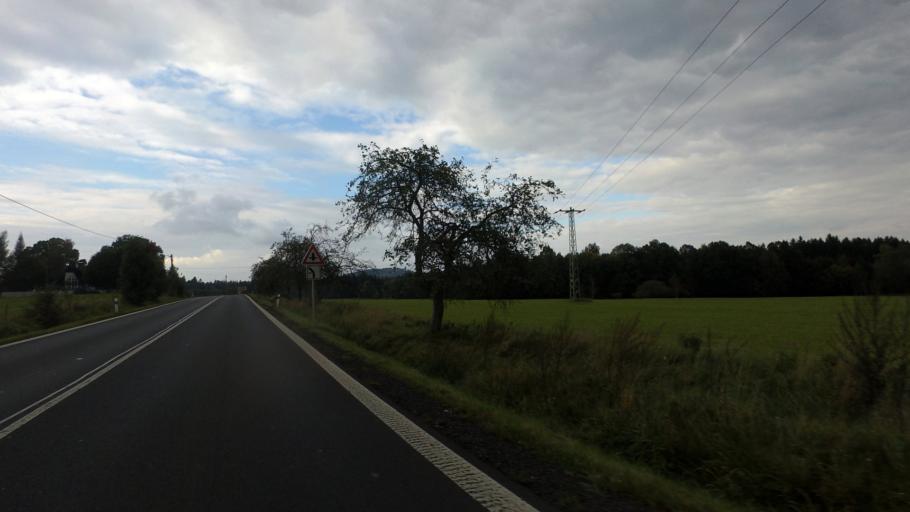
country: CZ
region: Ustecky
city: Stare Krecany
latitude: 50.9746
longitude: 14.5143
